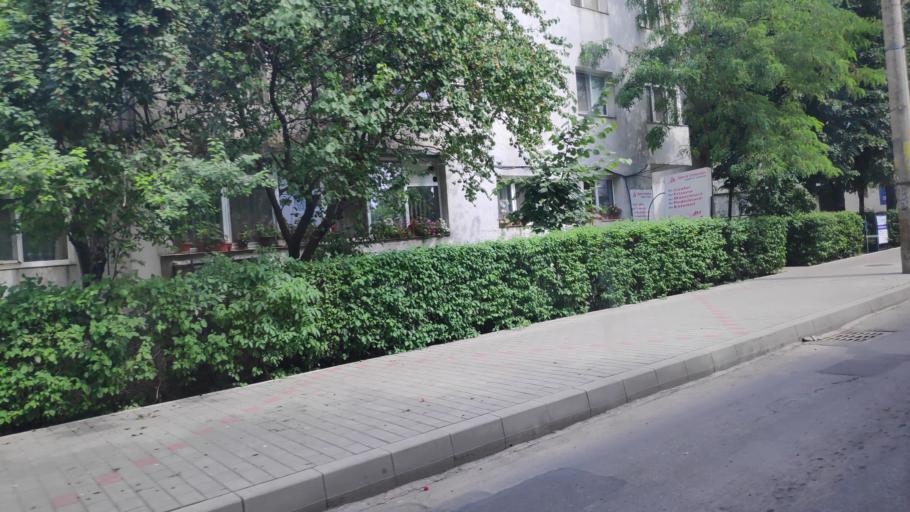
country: RO
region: Iasi
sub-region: Municipiul Iasi
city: Iasi
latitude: 47.1545
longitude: 27.5705
